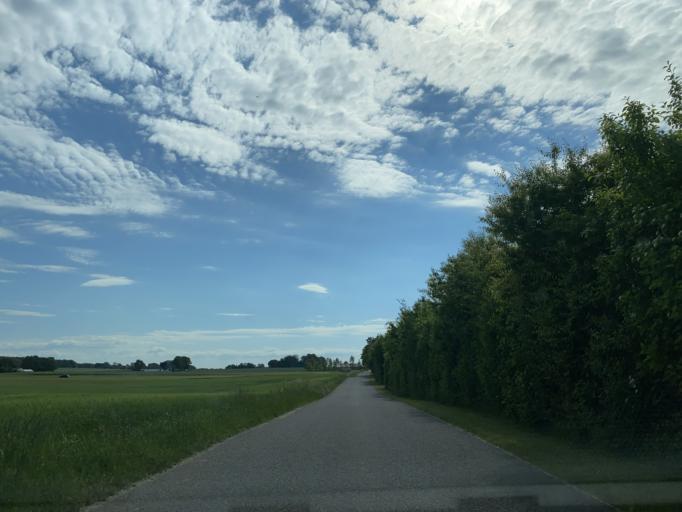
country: DK
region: Central Jutland
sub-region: Favrskov Kommune
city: Hammel
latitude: 56.2082
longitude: 9.8814
